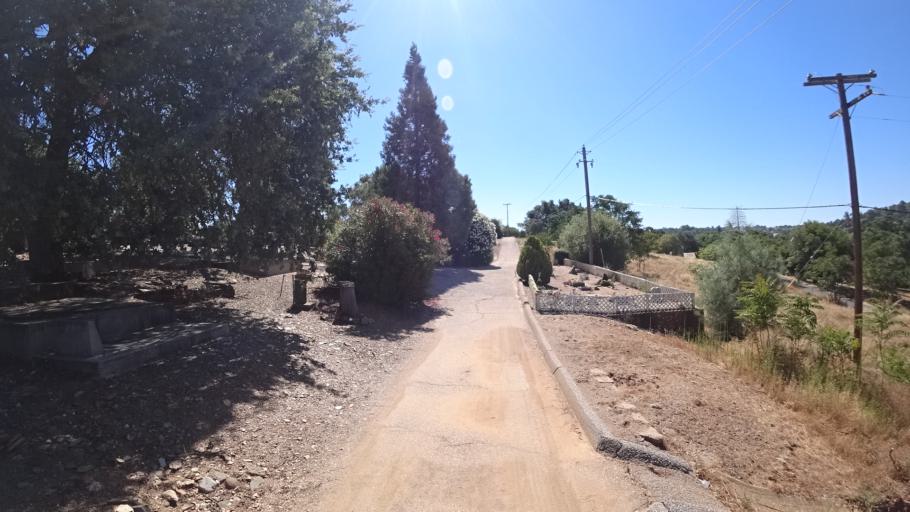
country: US
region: California
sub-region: Calaveras County
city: San Andreas
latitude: 38.2000
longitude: -120.6809
